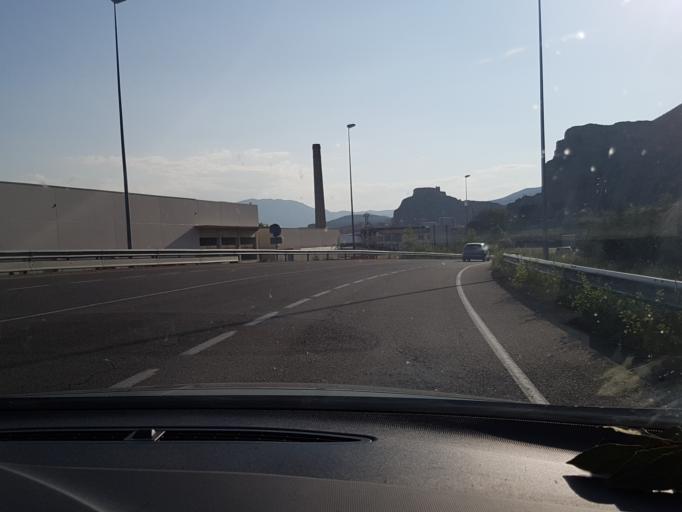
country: ES
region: La Rioja
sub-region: Provincia de La Rioja
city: Arnedo
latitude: 42.2313
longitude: -2.0792
